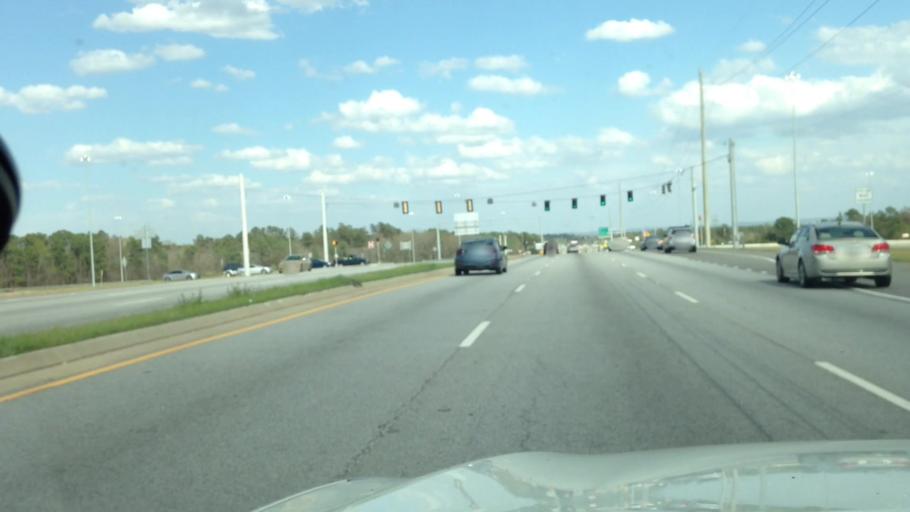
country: US
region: Georgia
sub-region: Columbia County
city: Martinez
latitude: 33.4501
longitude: -82.0766
